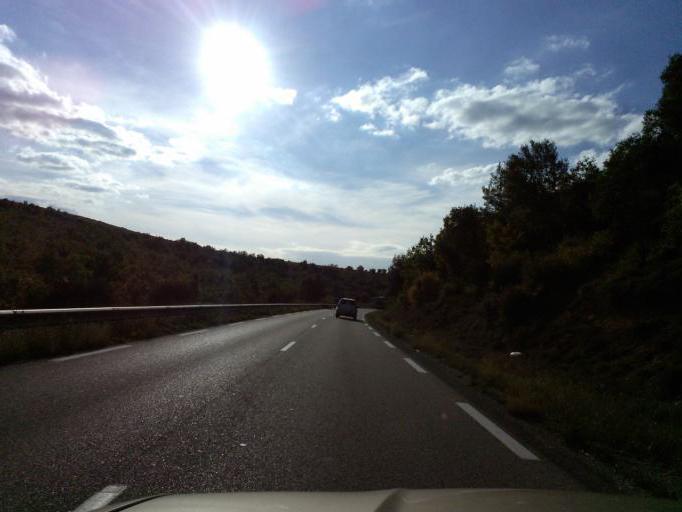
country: FR
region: Provence-Alpes-Cote d'Azur
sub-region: Departement des Alpes-de-Haute-Provence
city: Greoux-les-Bains
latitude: 43.7980
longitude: 5.8496
